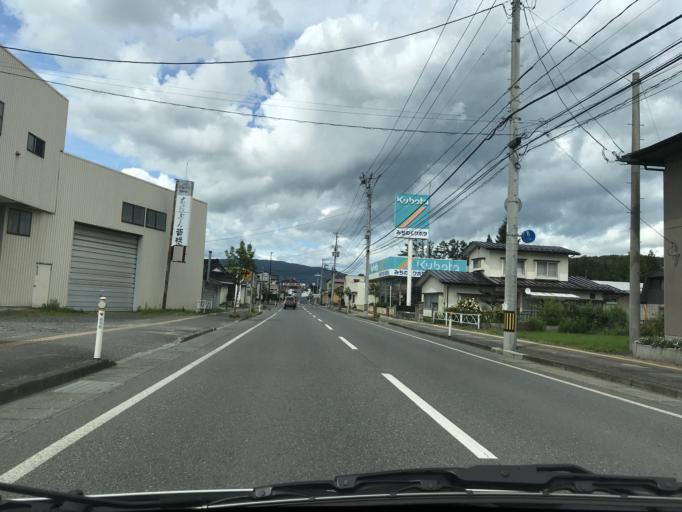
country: JP
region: Iwate
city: Tono
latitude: 39.3419
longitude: 141.5413
